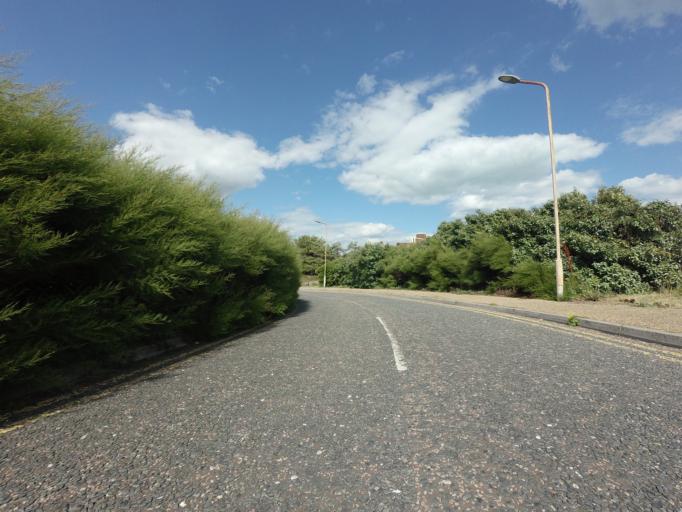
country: GB
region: England
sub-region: East Sussex
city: Pevensey
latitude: 50.7843
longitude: 0.3252
